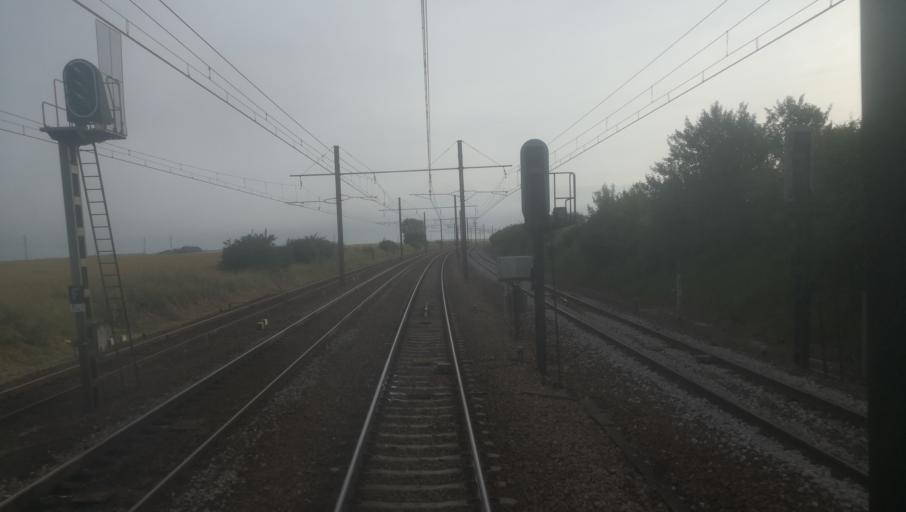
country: FR
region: Ile-de-France
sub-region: Departement de l'Essonne
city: Angerville
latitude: 48.3331
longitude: 2.0166
